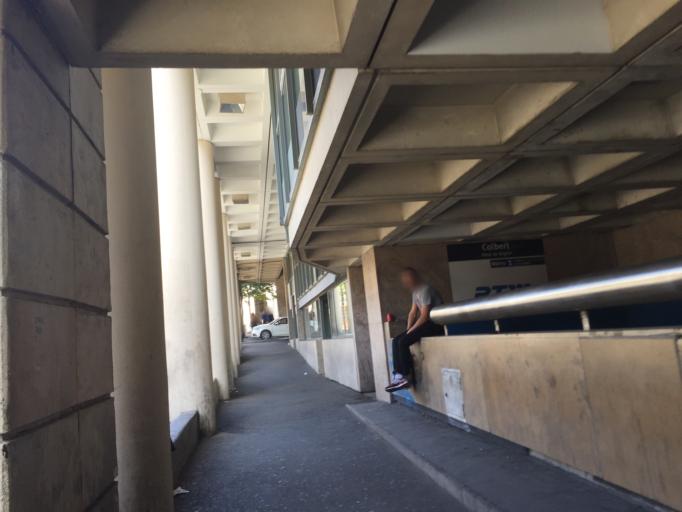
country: FR
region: Provence-Alpes-Cote d'Azur
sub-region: Departement des Bouches-du-Rhone
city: Marseille 03
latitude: 43.3000
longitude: 5.3744
